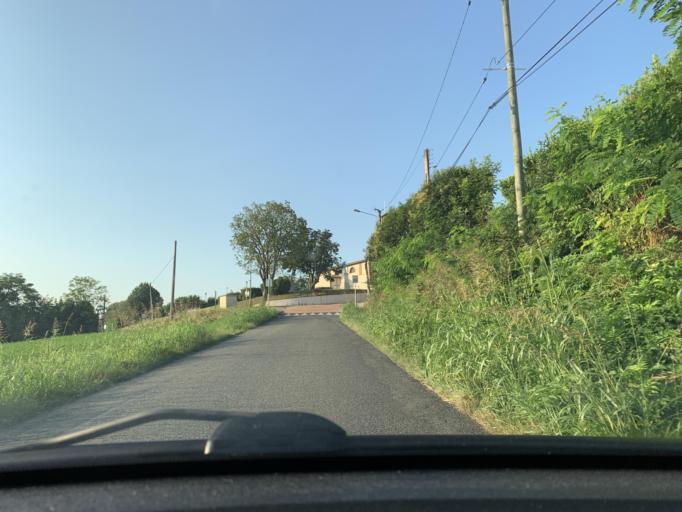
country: FR
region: Midi-Pyrenees
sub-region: Departement de la Haute-Garonne
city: Auzielle
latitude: 43.5251
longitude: 1.5897
